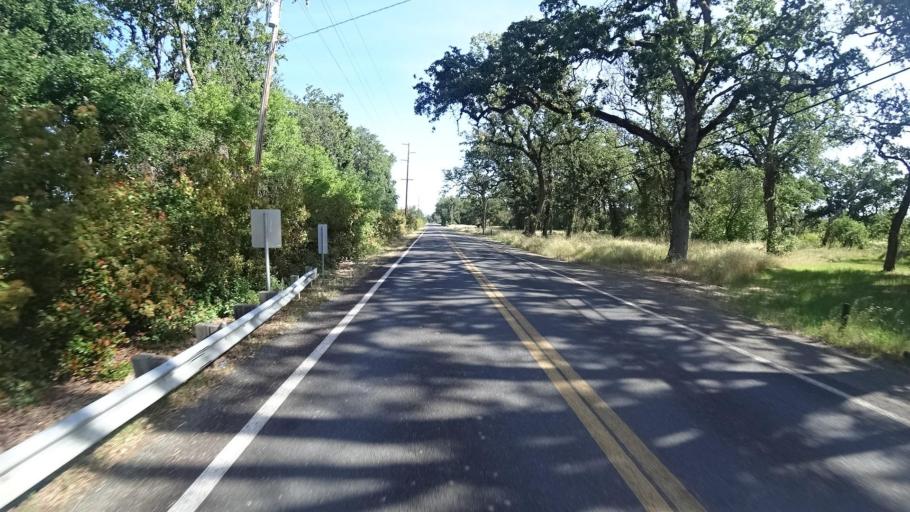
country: US
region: California
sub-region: Lake County
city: Lakeport
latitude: 38.9980
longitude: -122.8941
